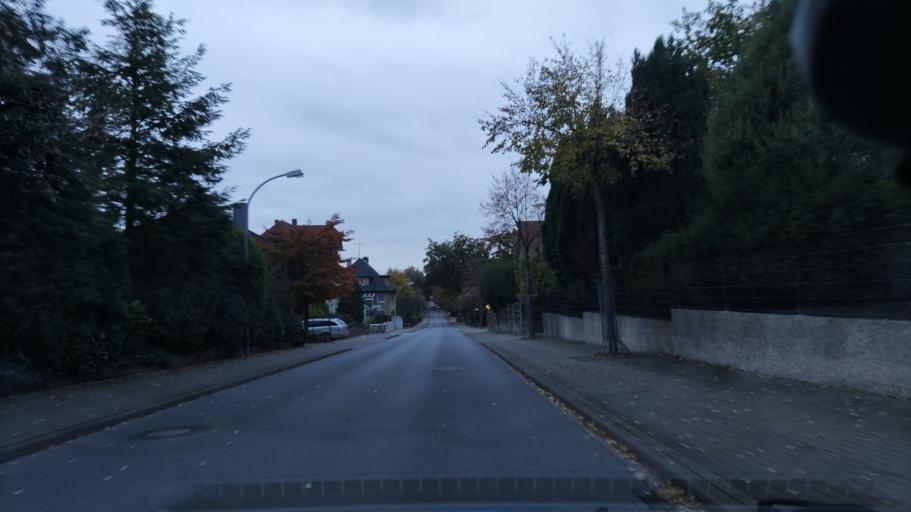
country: DE
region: Lower Saxony
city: Munster
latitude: 52.9923
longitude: 10.0902
